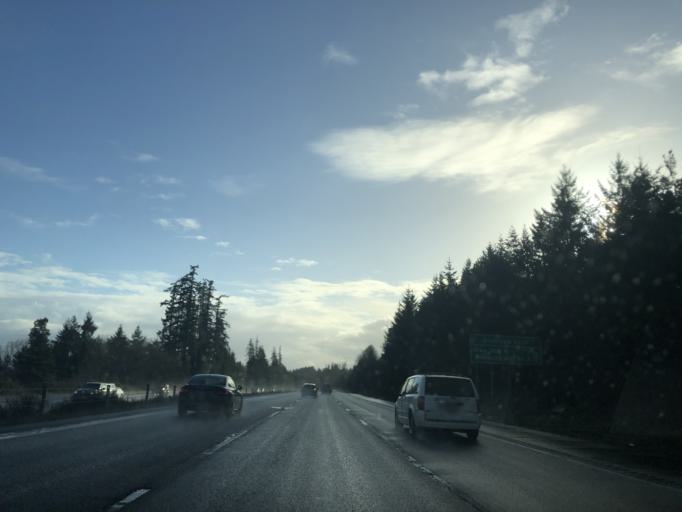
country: US
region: Washington
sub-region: Kitsap County
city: Silverdale
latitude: 47.6867
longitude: -122.6885
